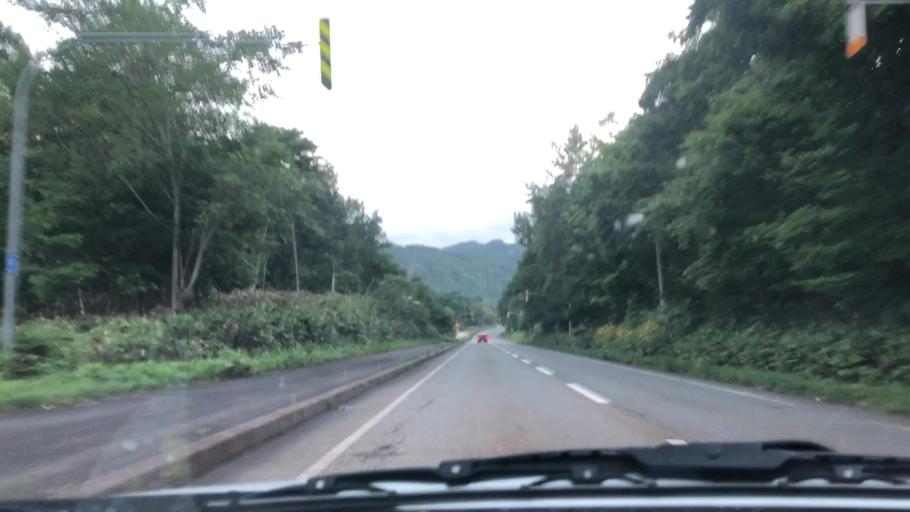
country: JP
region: Hokkaido
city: Chitose
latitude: 42.9095
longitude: 142.0167
